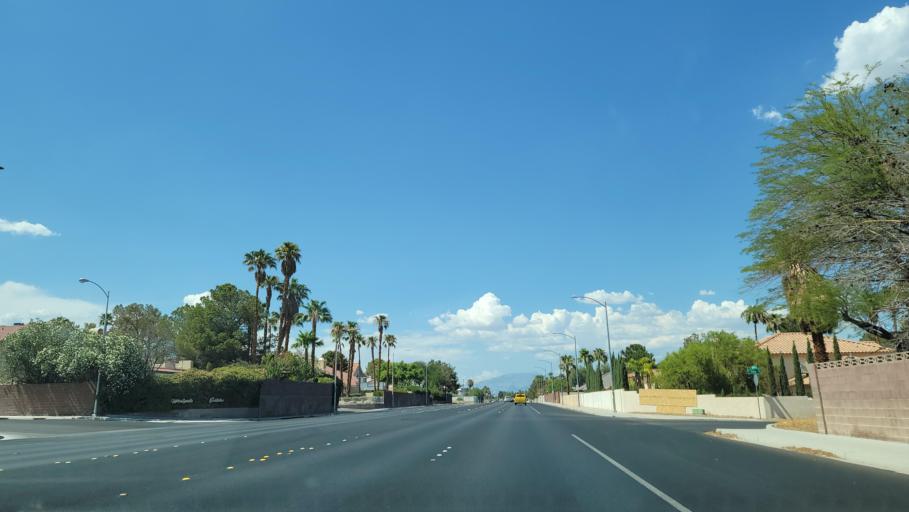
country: US
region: Nevada
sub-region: Clark County
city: Spring Valley
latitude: 36.1378
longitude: -115.2609
